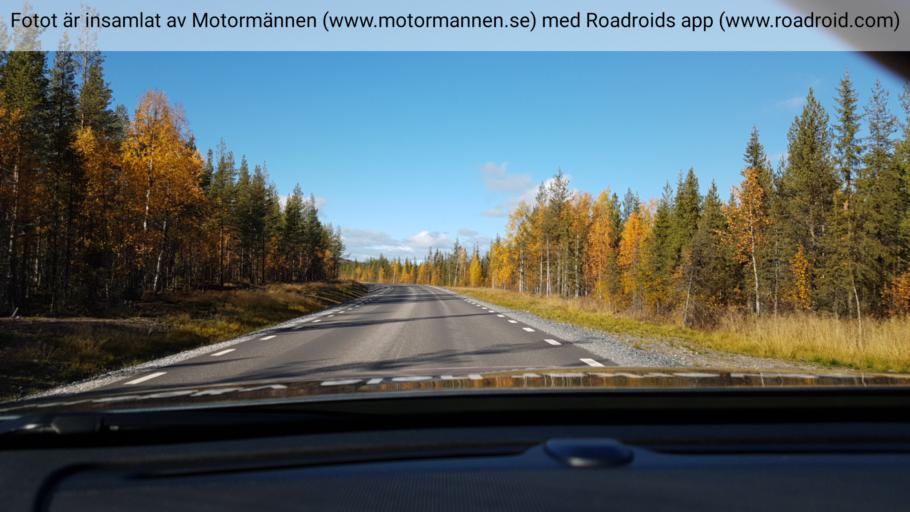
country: SE
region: Norrbotten
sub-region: Gallivare Kommun
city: Gaellivare
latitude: 67.0946
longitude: 20.7412
